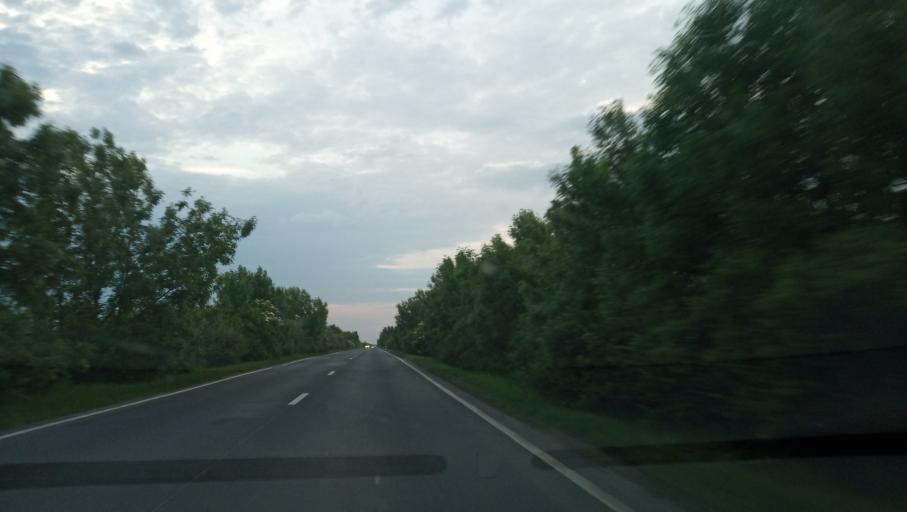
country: RO
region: Timis
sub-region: Comuna Jebel
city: Jebel
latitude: 45.5172
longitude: 21.2346
